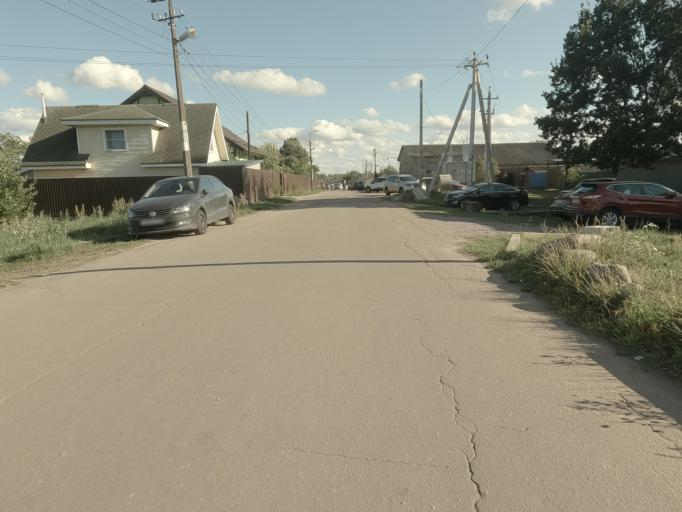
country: RU
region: Leningrad
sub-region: Volosovskiy Rayon
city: Shlissel'burg
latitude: 59.9593
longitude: 31.0312
